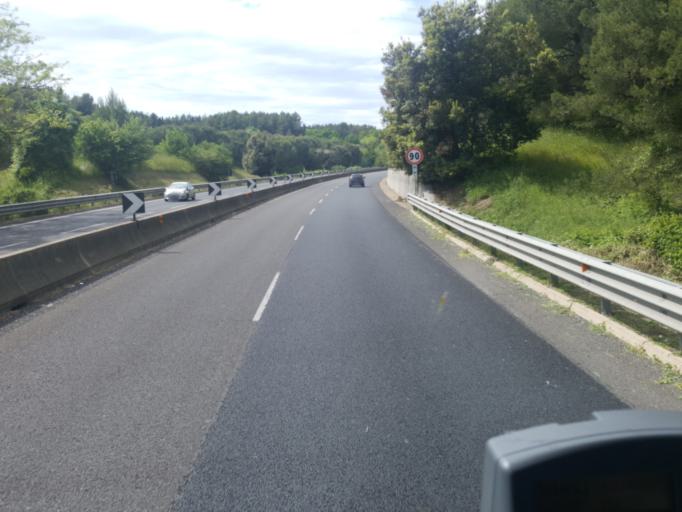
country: IT
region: Latium
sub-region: Citta metropolitana di Roma Capitale
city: Ara Nova
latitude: 41.8982
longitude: 12.2777
